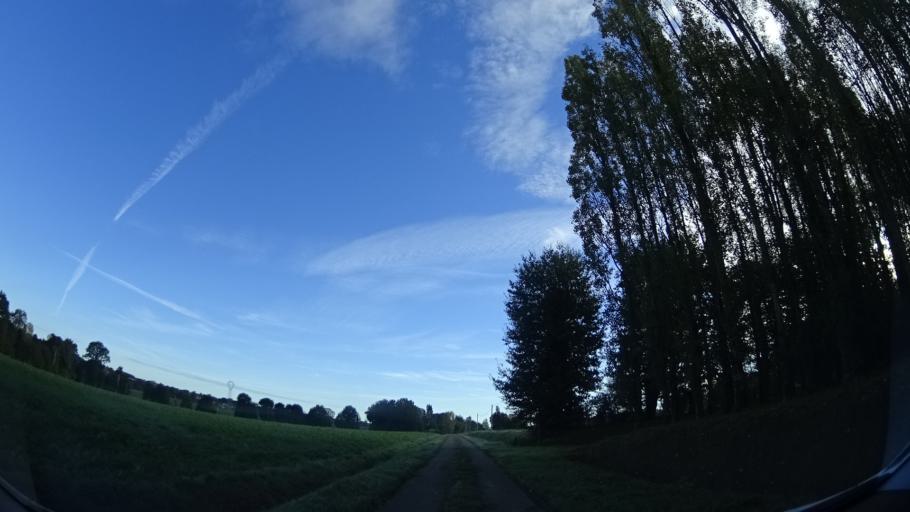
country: FR
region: Brittany
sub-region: Departement d'Ille-et-Vilaine
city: Geveze
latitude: 48.2120
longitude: -1.8102
